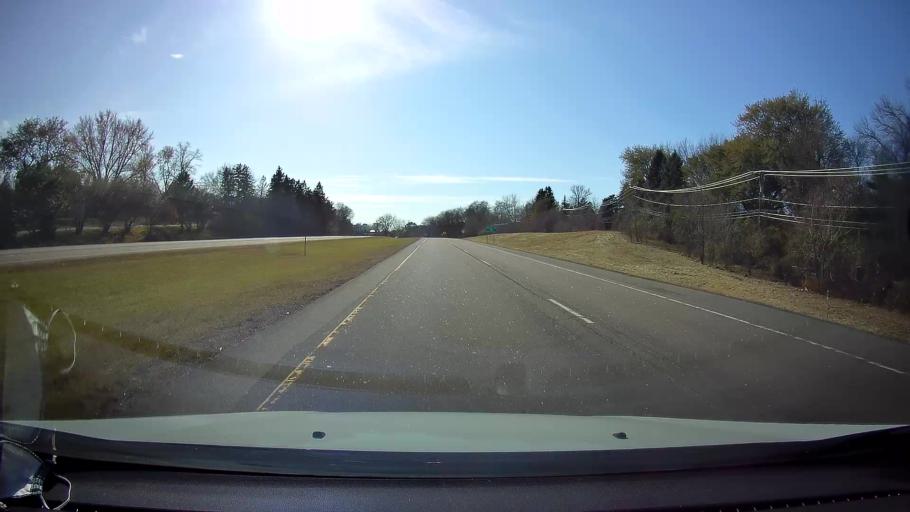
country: US
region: Minnesota
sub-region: Ramsey County
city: Arden Hills
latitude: 45.0355
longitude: -93.1633
